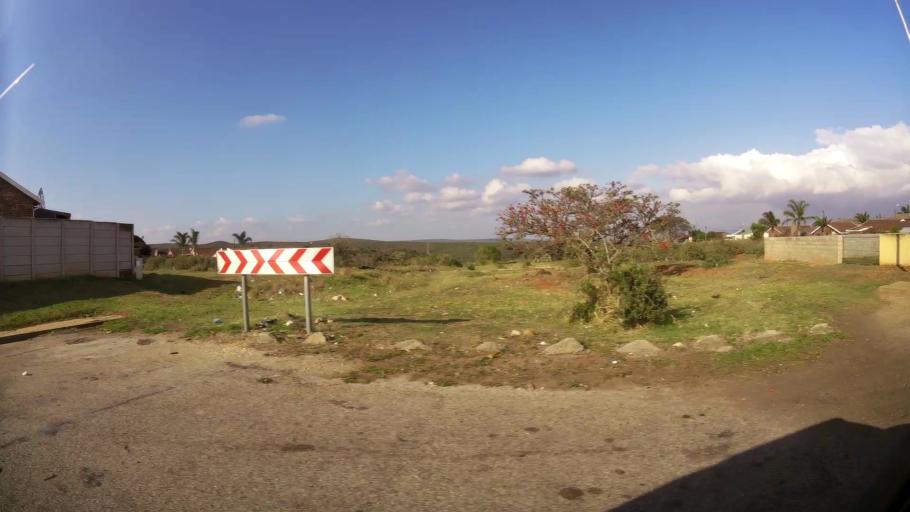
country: ZA
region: Eastern Cape
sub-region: Nelson Mandela Bay Metropolitan Municipality
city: Uitenhage
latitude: -33.7718
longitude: 25.4284
